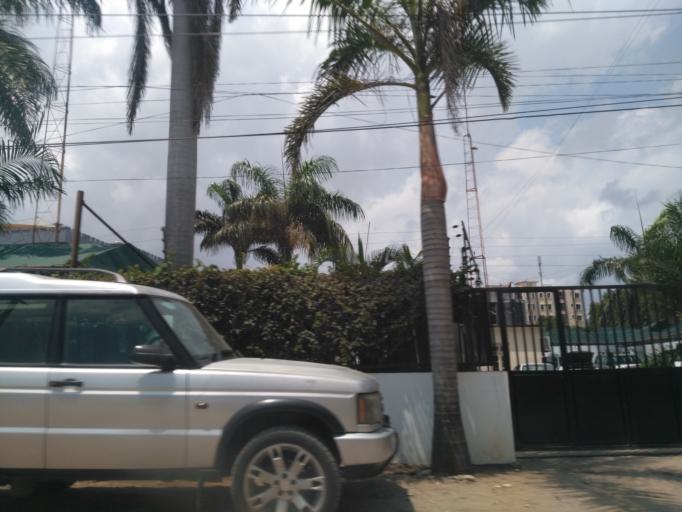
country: TZ
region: Dar es Salaam
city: Dar es Salaam
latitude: -6.8014
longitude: 39.2797
